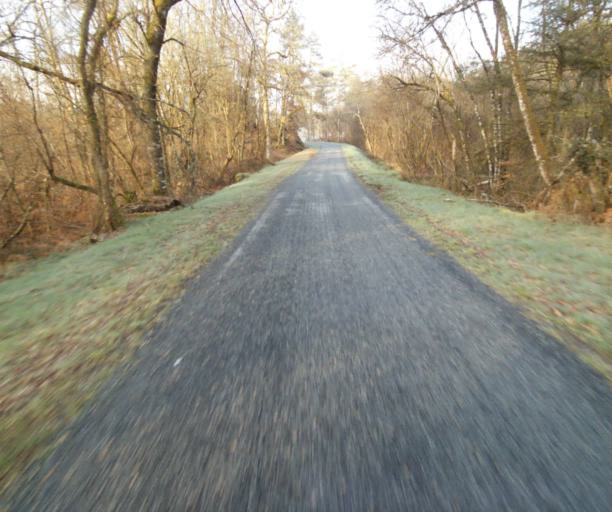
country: FR
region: Limousin
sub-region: Departement de la Correze
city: Correze
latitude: 45.3158
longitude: 1.8598
